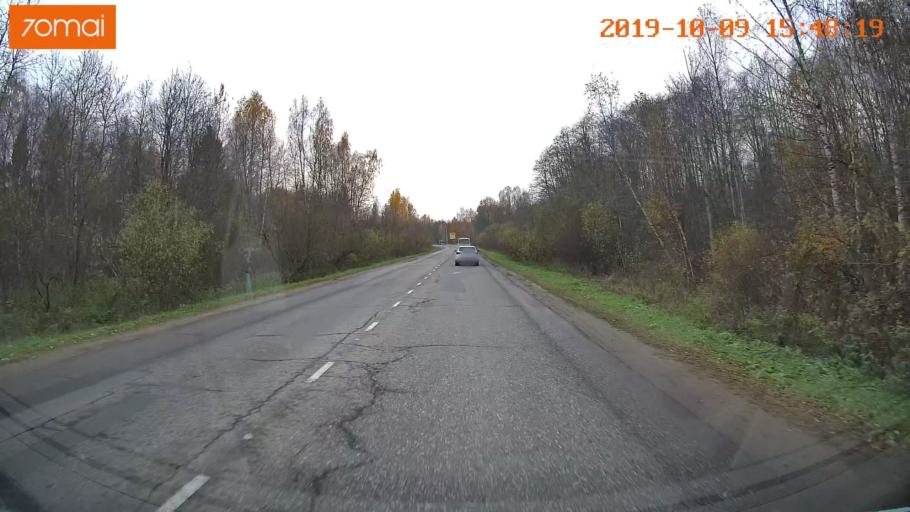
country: RU
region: Kostroma
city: Oktyabr'skiy
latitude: 57.8124
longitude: 41.0167
